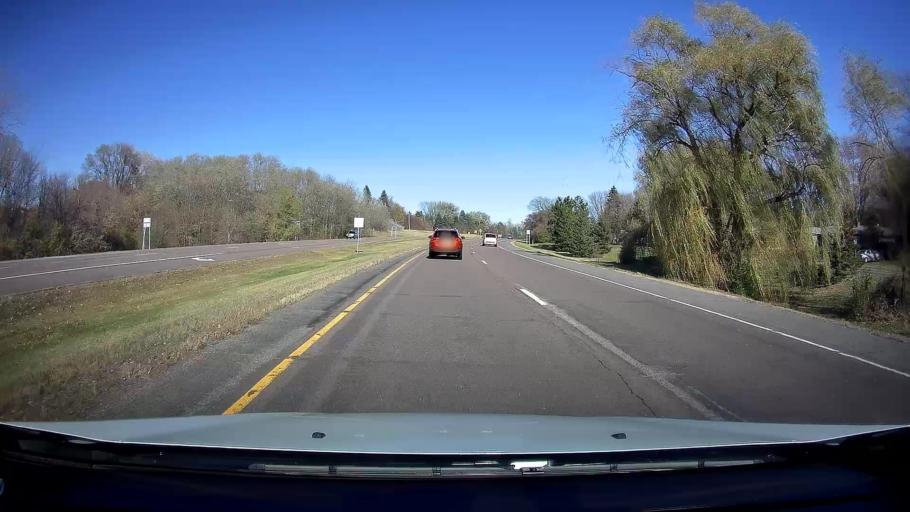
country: US
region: Minnesota
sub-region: Ramsey County
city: Arden Hills
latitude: 45.0316
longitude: -93.1666
